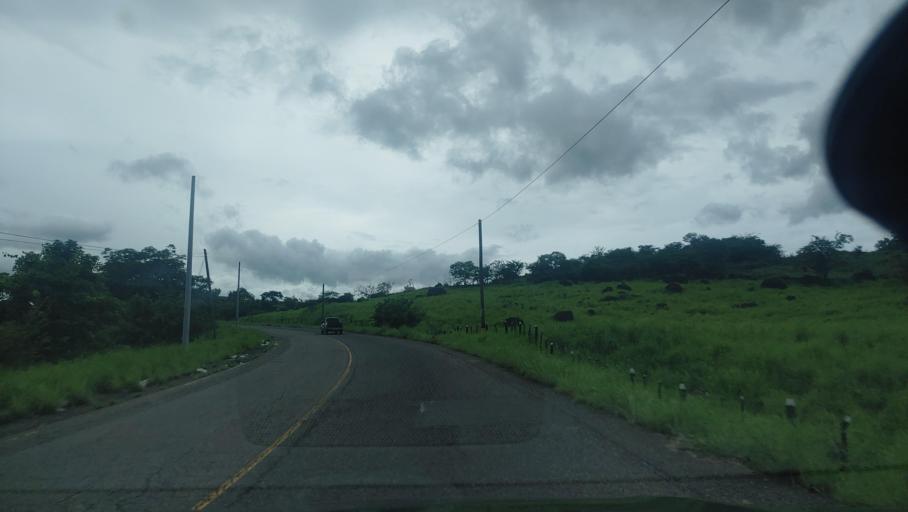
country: HN
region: Choluteca
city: Corpus
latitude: 13.3747
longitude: -87.0599
